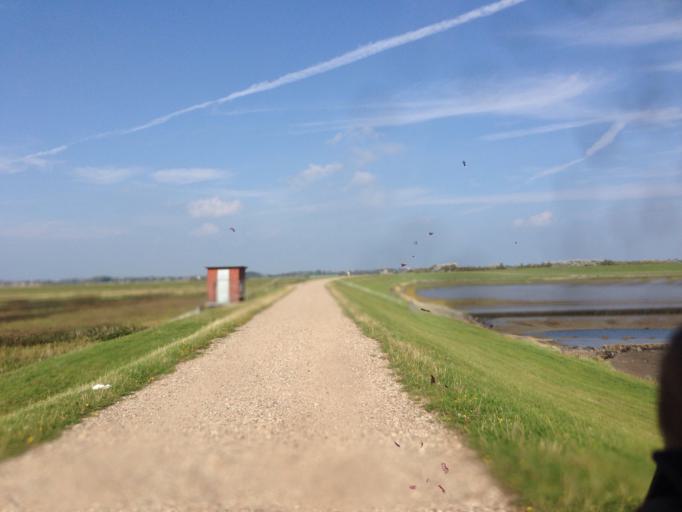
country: DE
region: Schleswig-Holstein
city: Tinnum
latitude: 54.8788
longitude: 8.3373
